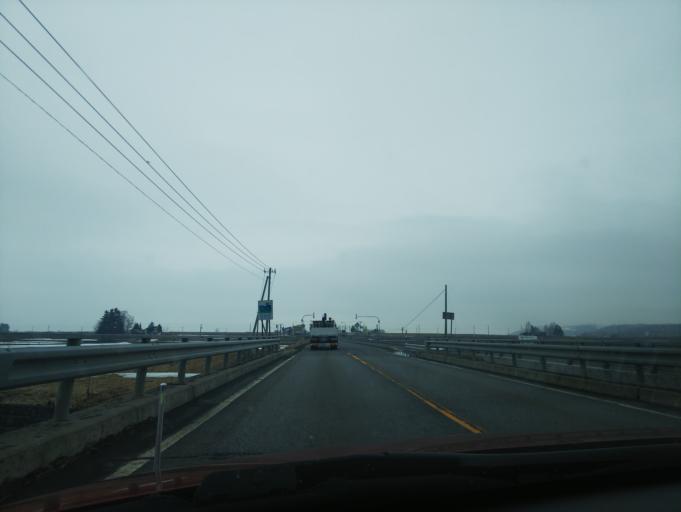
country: JP
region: Hokkaido
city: Nayoro
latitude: 44.0677
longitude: 142.3968
